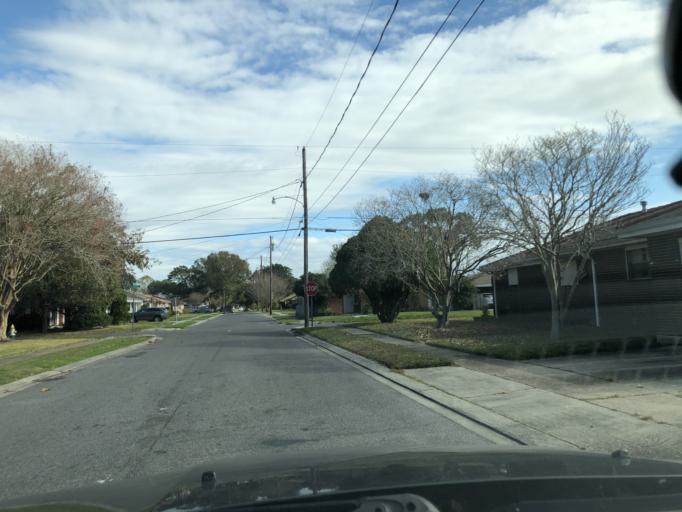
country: US
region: Louisiana
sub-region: Jefferson Parish
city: Metairie Terrace
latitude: 29.9855
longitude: -90.1634
